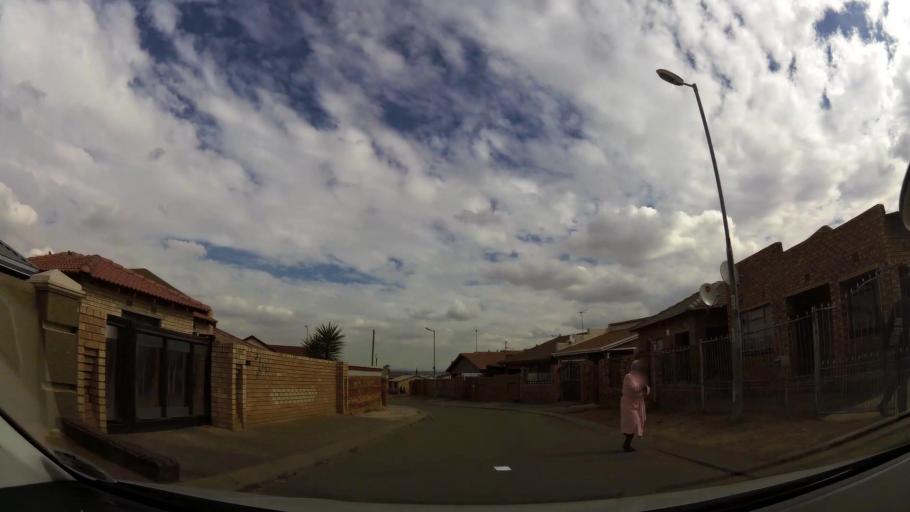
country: ZA
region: Gauteng
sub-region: City of Johannesburg Metropolitan Municipality
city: Soweto
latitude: -26.2760
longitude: 27.8490
